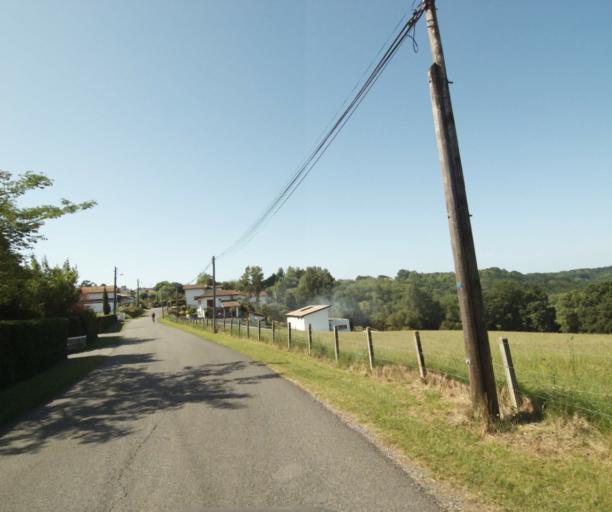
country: FR
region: Aquitaine
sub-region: Departement des Pyrenees-Atlantiques
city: Villefranque
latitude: 43.4614
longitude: -1.4487
